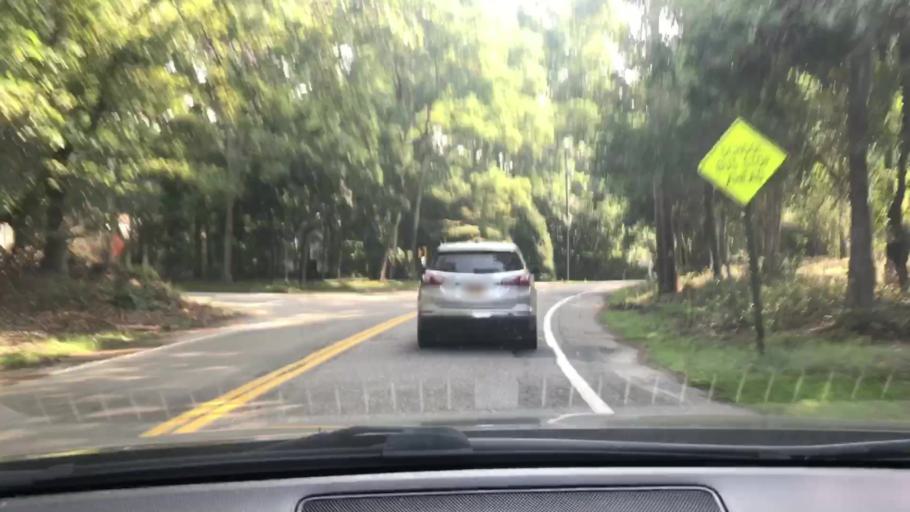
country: US
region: New York
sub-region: Suffolk County
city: Noyack
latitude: 40.9803
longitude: -72.3187
